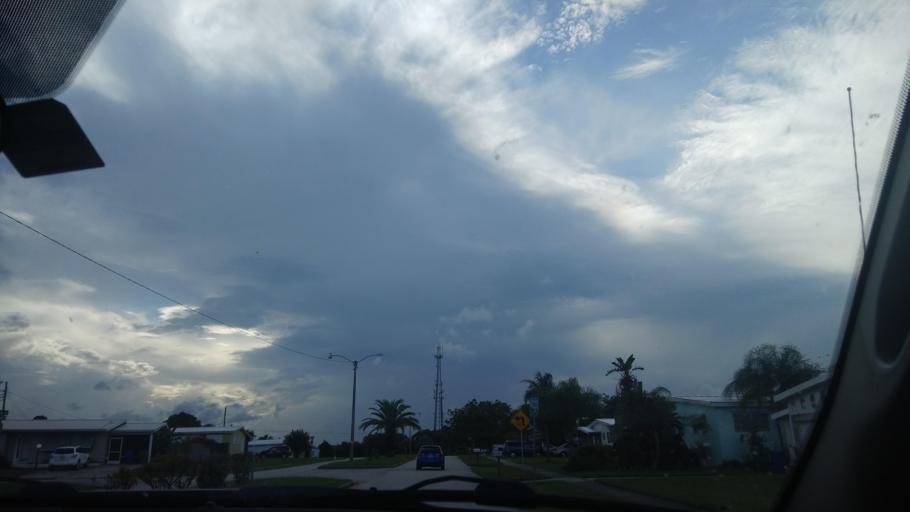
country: US
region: Florida
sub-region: Indian River County
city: Sebastian
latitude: 27.7879
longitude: -80.4599
